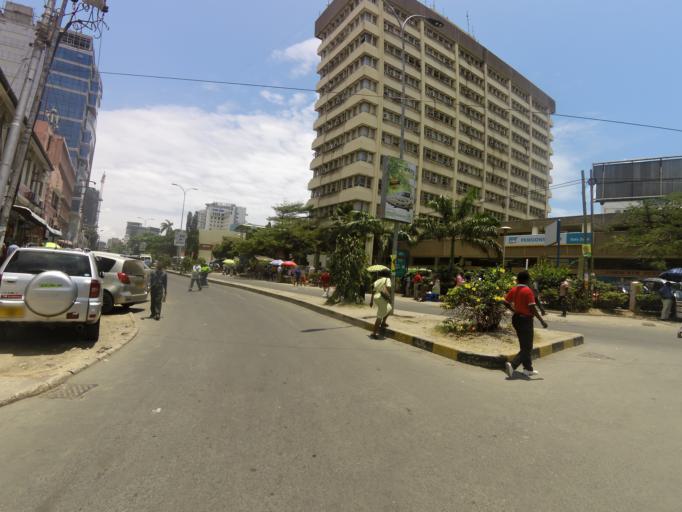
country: TZ
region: Dar es Salaam
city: Dar es Salaam
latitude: -6.8165
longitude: 39.2894
